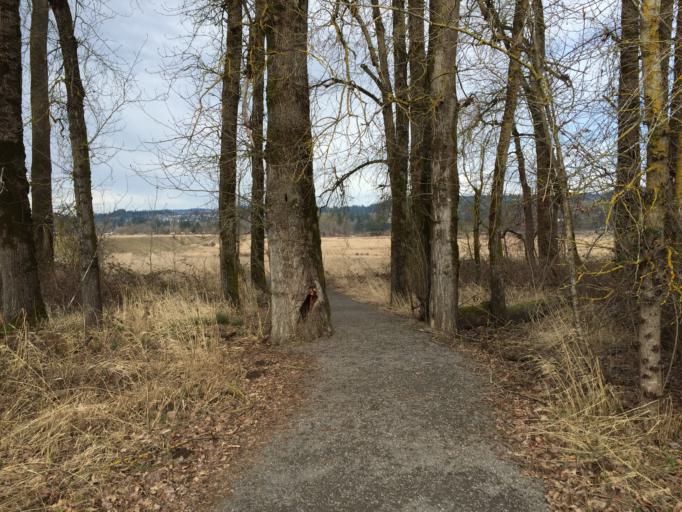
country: US
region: Washington
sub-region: Clark County
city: Washougal
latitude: 45.5643
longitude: -122.3142
